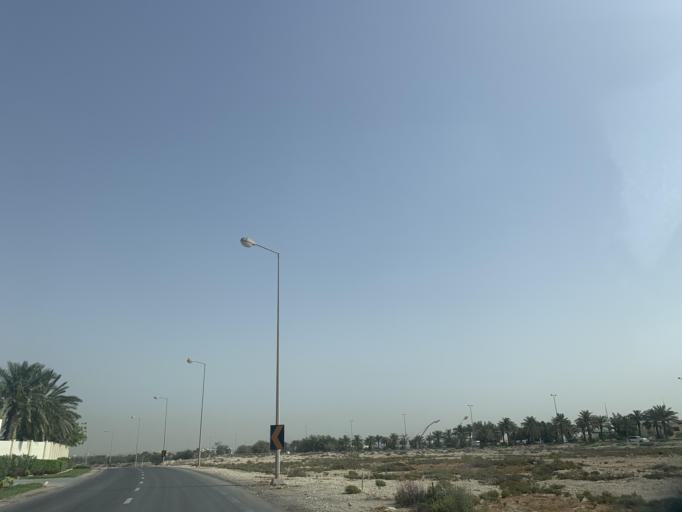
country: BH
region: Northern
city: Ar Rifa'
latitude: 26.1448
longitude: 50.5387
